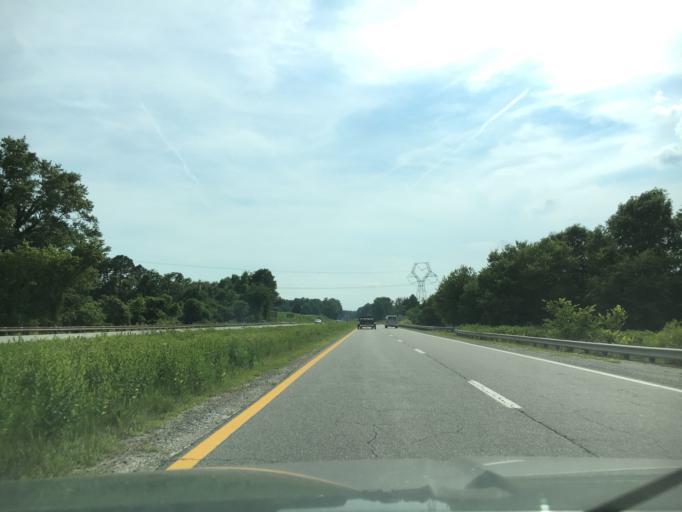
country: US
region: Virginia
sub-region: Mecklenburg County
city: Chase City
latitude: 36.8650
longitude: -78.5856
